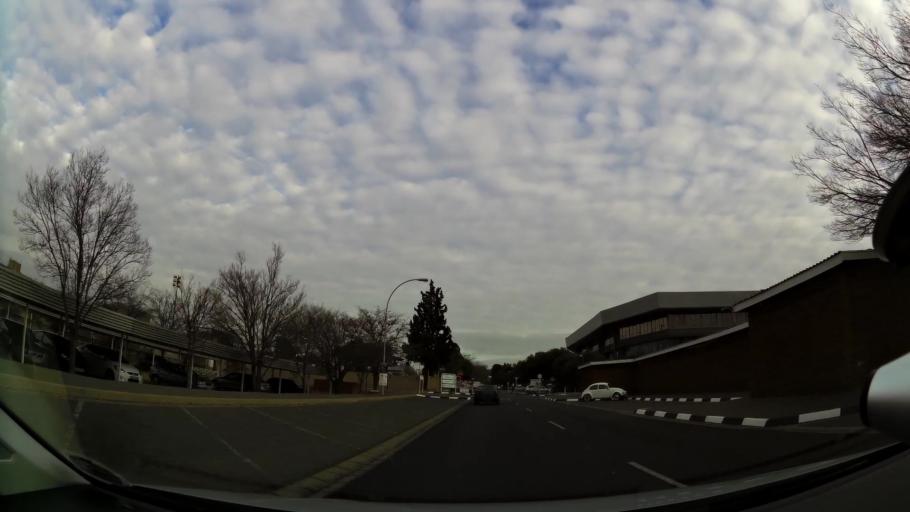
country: ZA
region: Orange Free State
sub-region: Mangaung Metropolitan Municipality
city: Bloemfontein
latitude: -29.1136
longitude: 26.1896
